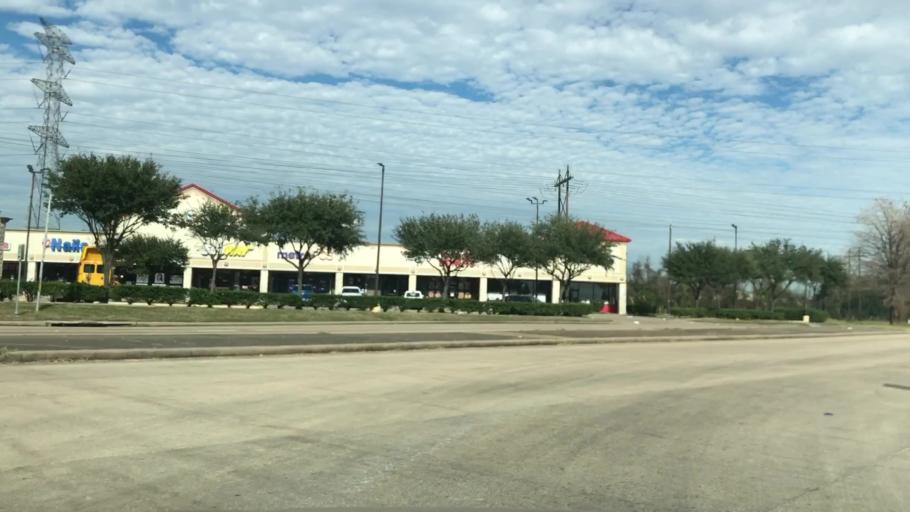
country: US
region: Texas
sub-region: Fort Bend County
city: Missouri City
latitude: 29.6212
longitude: -95.5082
